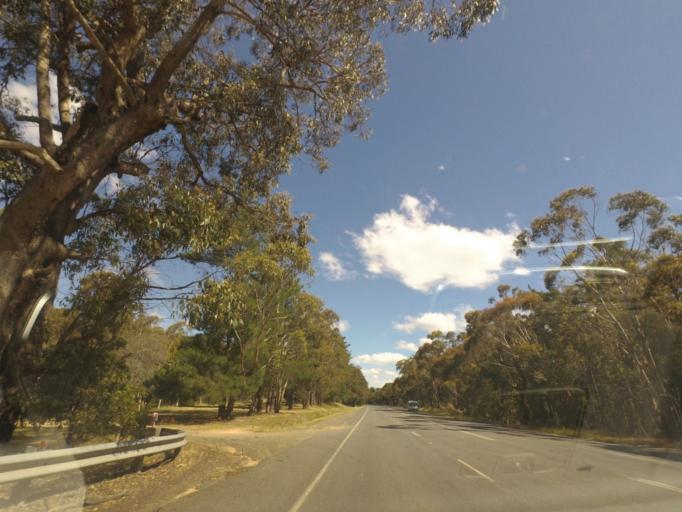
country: AU
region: Victoria
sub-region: Hume
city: Sunbury
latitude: -37.4248
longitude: 144.5541
